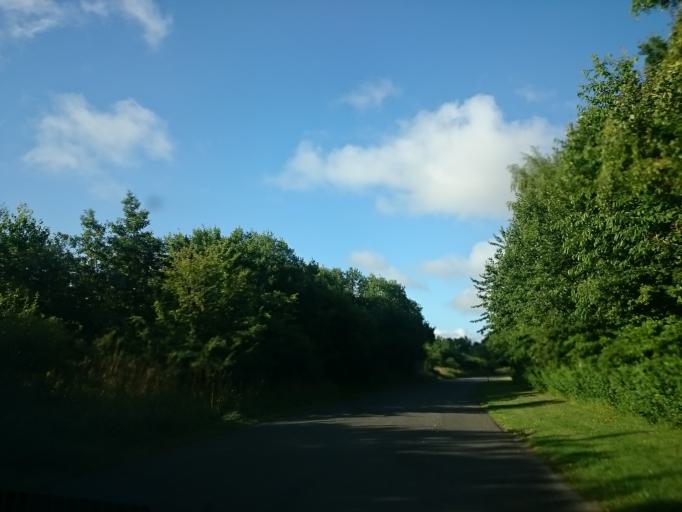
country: DK
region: Central Jutland
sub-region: Arhus Kommune
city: Stavtrup
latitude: 56.1126
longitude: 10.1065
